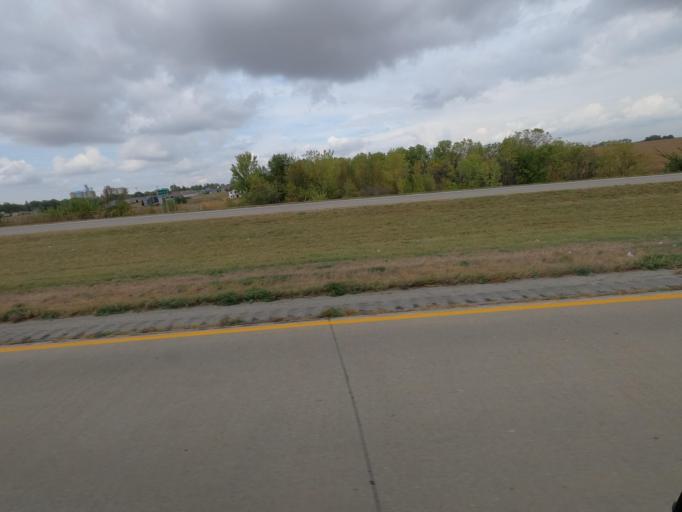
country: US
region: Iowa
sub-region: Jasper County
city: Prairie City
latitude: 41.5881
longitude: -93.2289
